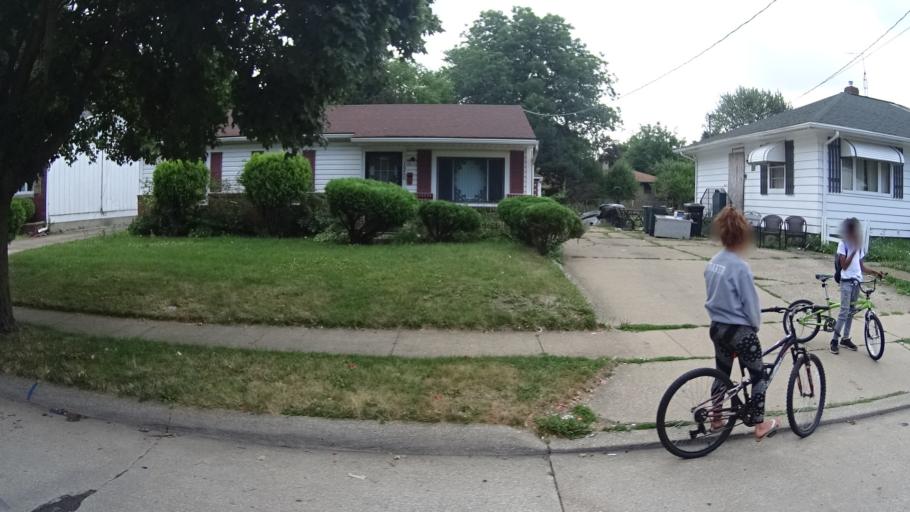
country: US
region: Ohio
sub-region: Erie County
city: Sandusky
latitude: 41.4370
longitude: -82.7246
